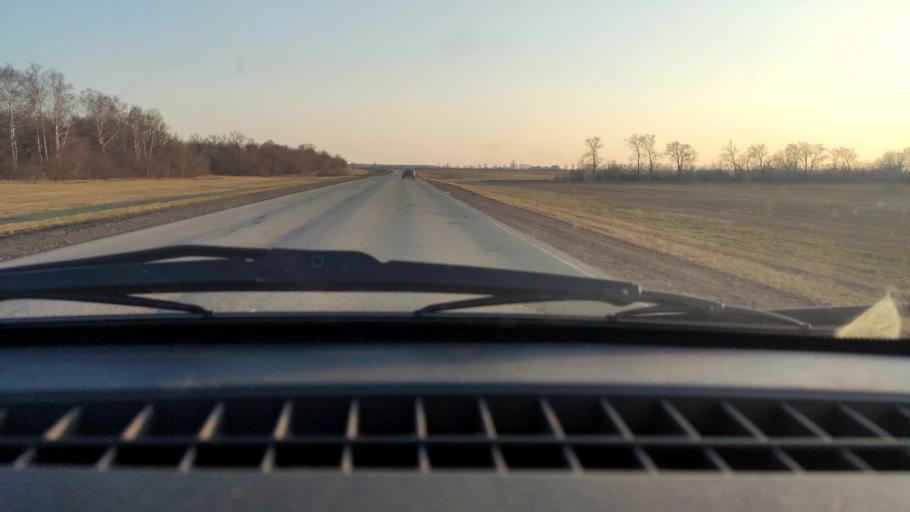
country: RU
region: Bashkortostan
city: Davlekanovo
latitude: 54.2820
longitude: 55.1101
